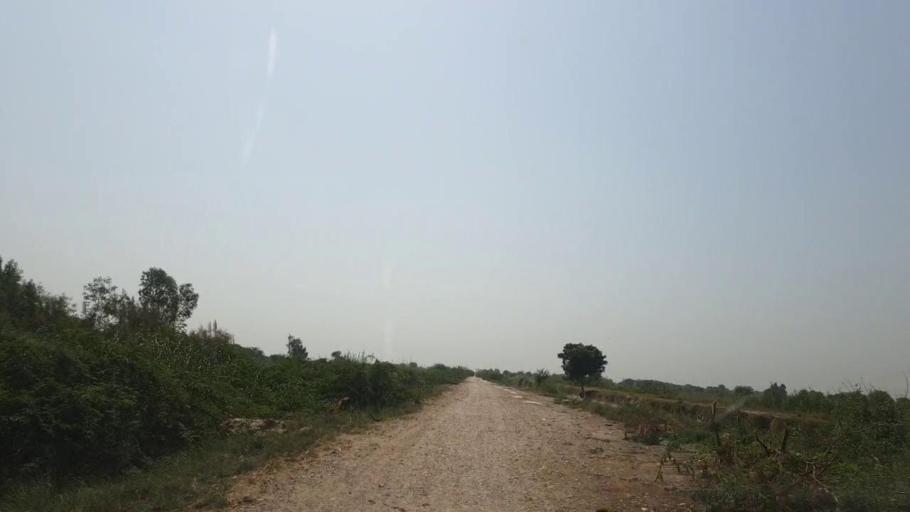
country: PK
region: Sindh
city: Jhol
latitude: 25.8814
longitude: 69.0372
